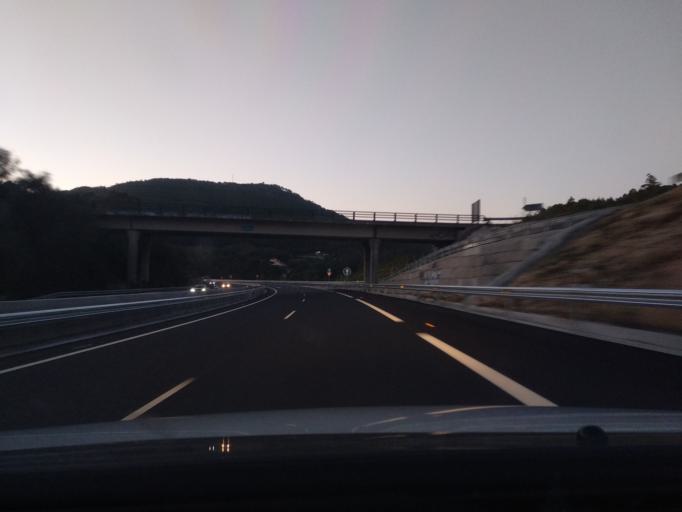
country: ES
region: Galicia
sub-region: Provincia de Pontevedra
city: Moana
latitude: 42.3048
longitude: -8.7198
